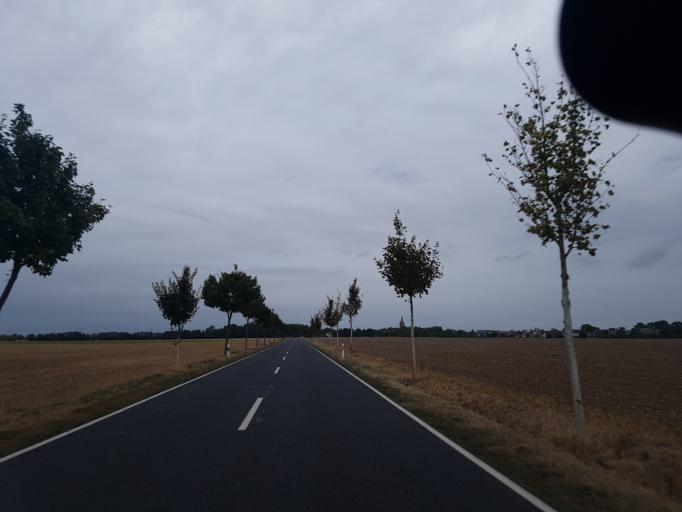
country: DE
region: Saxony-Anhalt
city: Prettin
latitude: 51.6924
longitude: 12.8936
